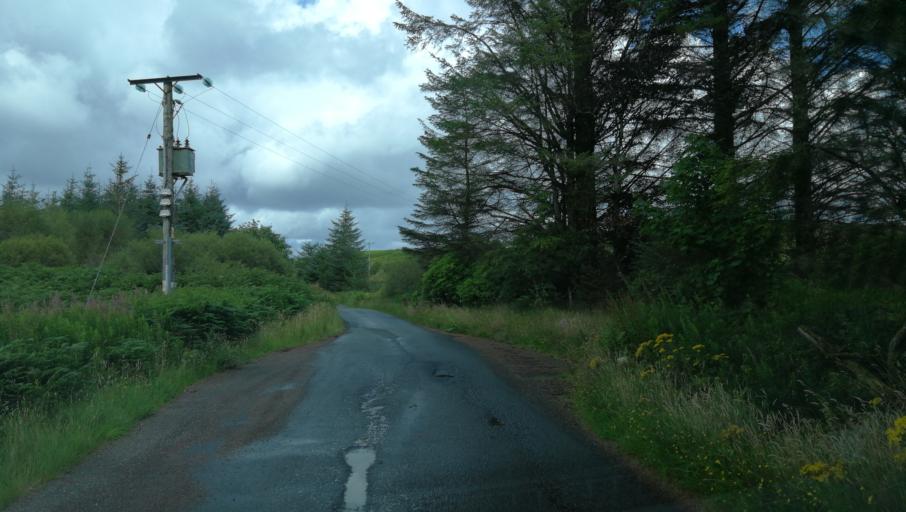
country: GB
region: Scotland
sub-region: Highland
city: Portree
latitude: 57.3805
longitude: -6.1947
